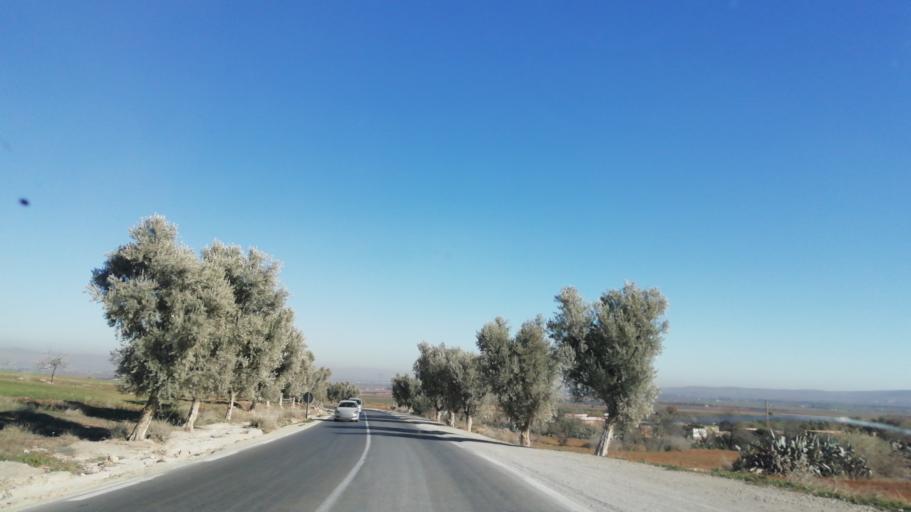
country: DZ
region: Mascara
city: Mascara
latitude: 35.2539
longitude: 0.1242
